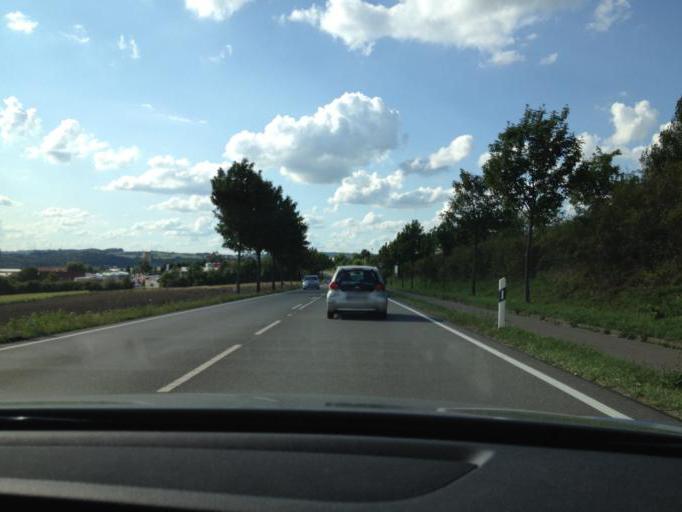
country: DE
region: Saarland
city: Schmelz
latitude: 49.4380
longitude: 6.8779
